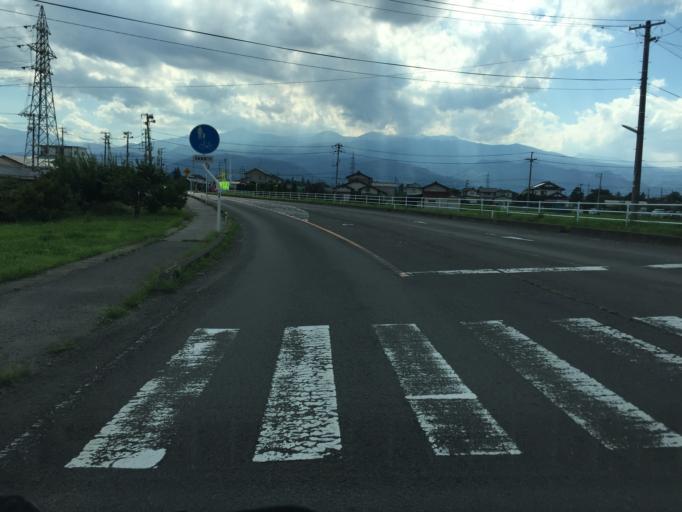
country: JP
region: Fukushima
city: Fukushima-shi
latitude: 37.7513
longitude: 140.4173
